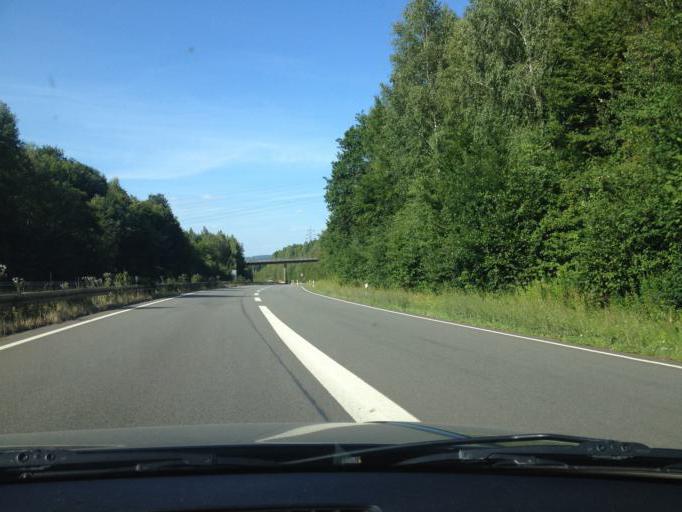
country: DE
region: Saarland
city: Spiesen-Elversberg
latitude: 49.3265
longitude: 7.1588
